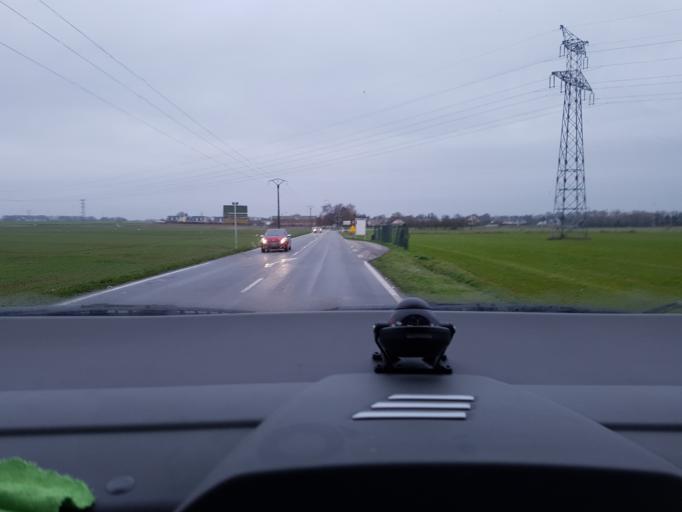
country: FR
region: Haute-Normandie
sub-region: Departement de l'Eure
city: Le Neubourg
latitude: 49.1389
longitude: 0.8882
